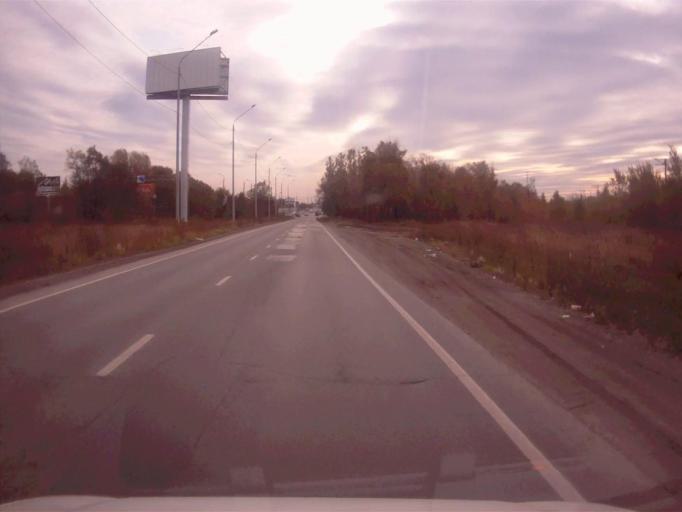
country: RU
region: Chelyabinsk
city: Novosineglazovskiy
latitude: 55.0798
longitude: 61.3879
